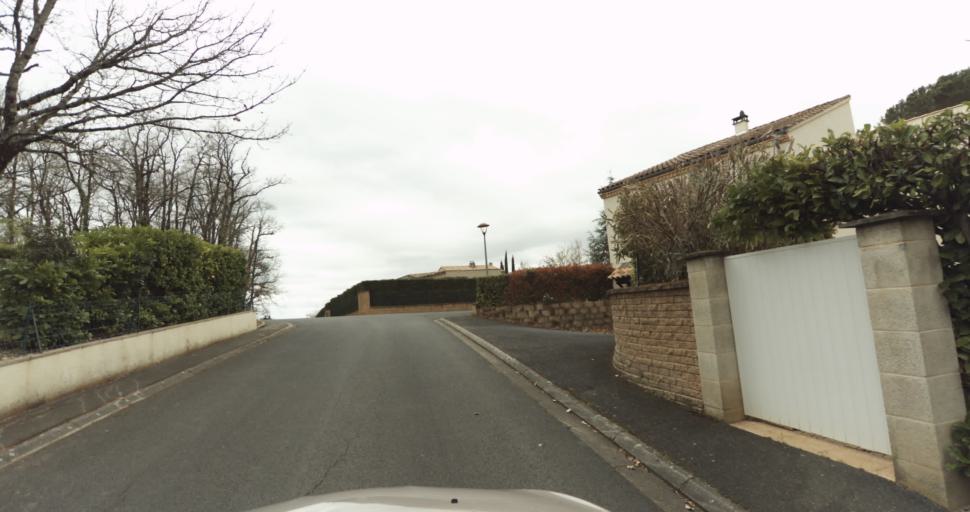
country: FR
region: Midi-Pyrenees
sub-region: Departement du Tarn
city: Puygouzon
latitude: 43.9044
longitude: 2.1641
